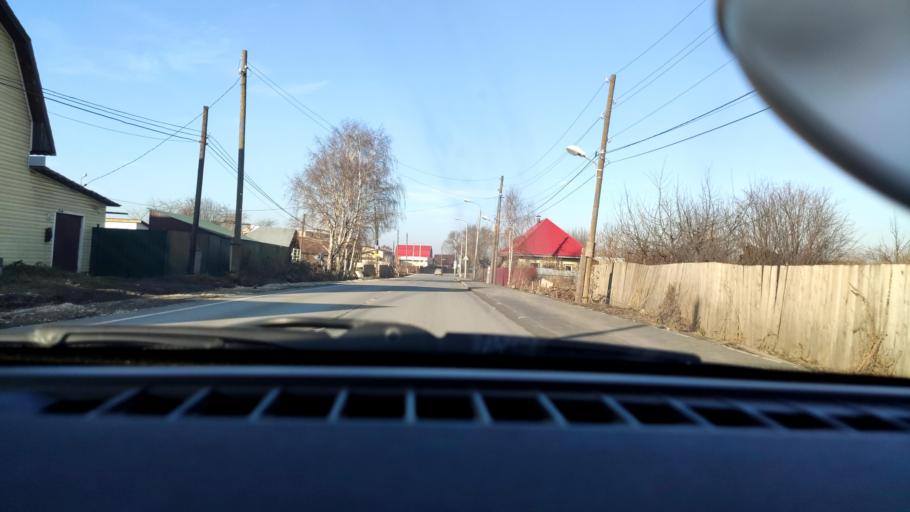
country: RU
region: Perm
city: Kondratovo
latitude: 57.9610
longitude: 56.1248
